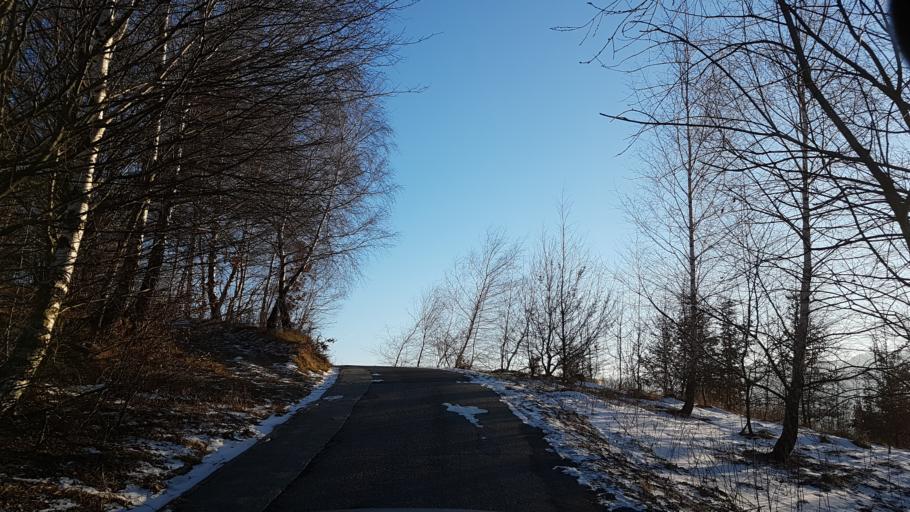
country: PL
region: Lesser Poland Voivodeship
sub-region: Powiat nowosadecki
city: Rytro
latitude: 49.5089
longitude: 20.6723
